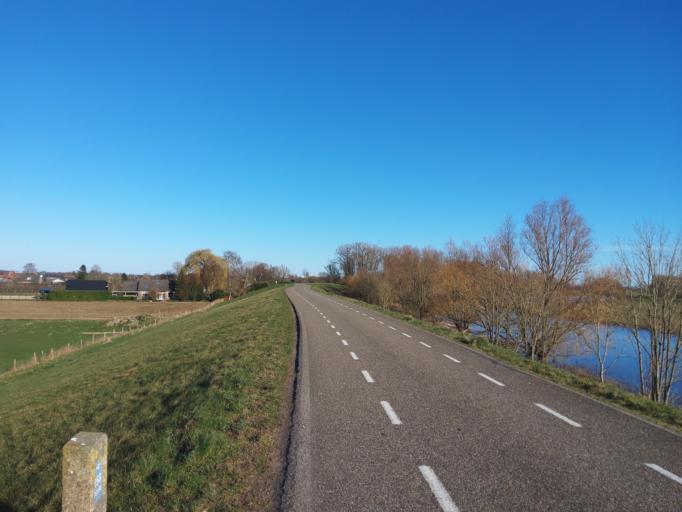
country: NL
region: Gelderland
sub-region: Gemeente Neerijnen
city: Neerijnen
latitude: 51.8284
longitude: 5.3127
